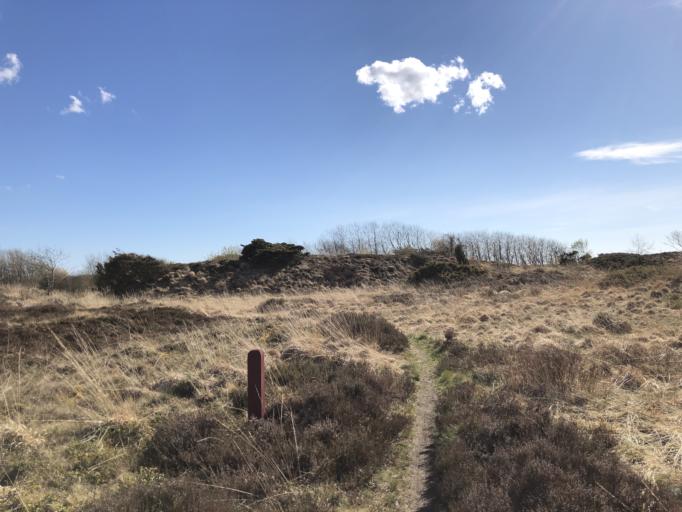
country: DK
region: Central Jutland
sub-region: Holstebro Kommune
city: Ulfborg
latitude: 56.2521
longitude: 8.4121
